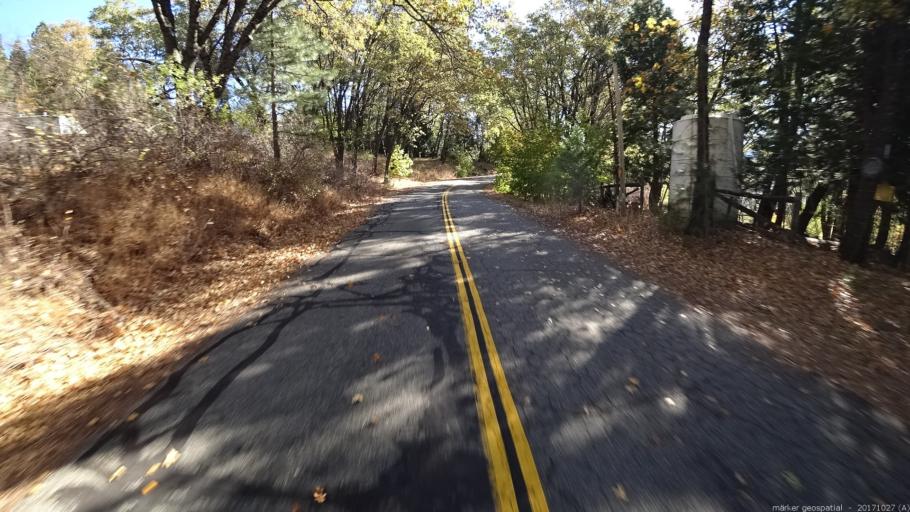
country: US
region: California
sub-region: Shasta County
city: Burney
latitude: 40.8483
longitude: -121.9107
